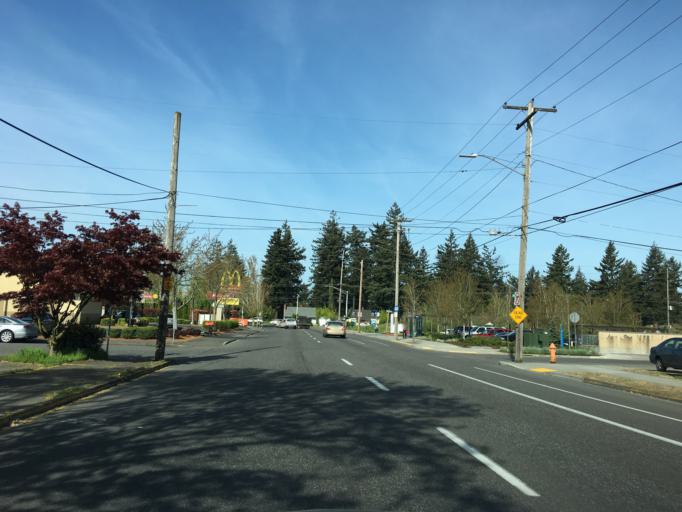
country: US
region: Oregon
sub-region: Multnomah County
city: Lents
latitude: 45.5342
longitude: -122.5562
